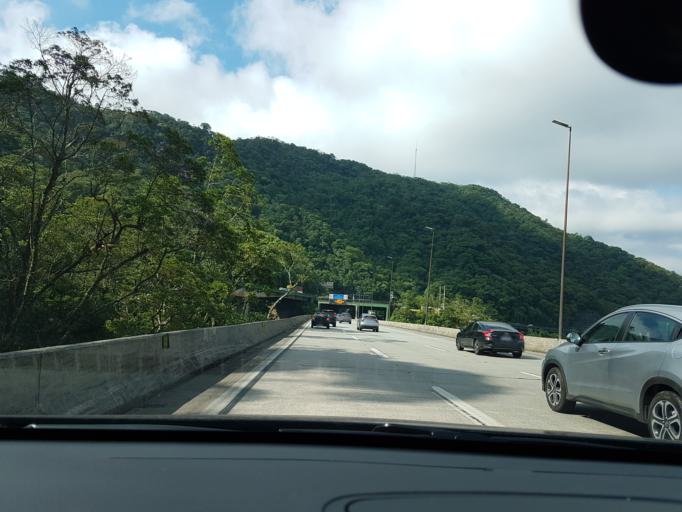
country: BR
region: Sao Paulo
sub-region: Cubatao
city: Cubatao
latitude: -23.9211
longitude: -46.5315
